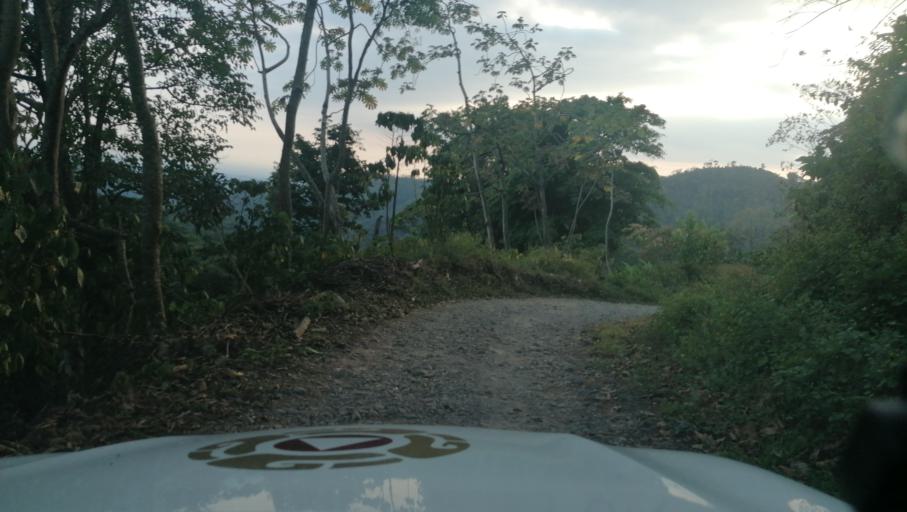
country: MX
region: Chiapas
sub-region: Cacahoatan
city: Benito Juarez
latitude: 15.0957
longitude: -92.2209
